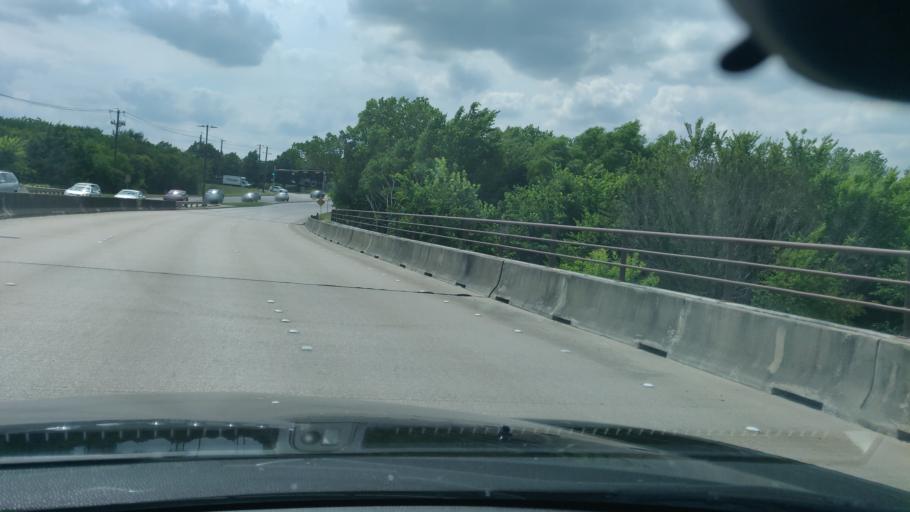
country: US
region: Texas
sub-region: Dallas County
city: Rowlett
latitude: 32.9314
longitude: -96.5949
